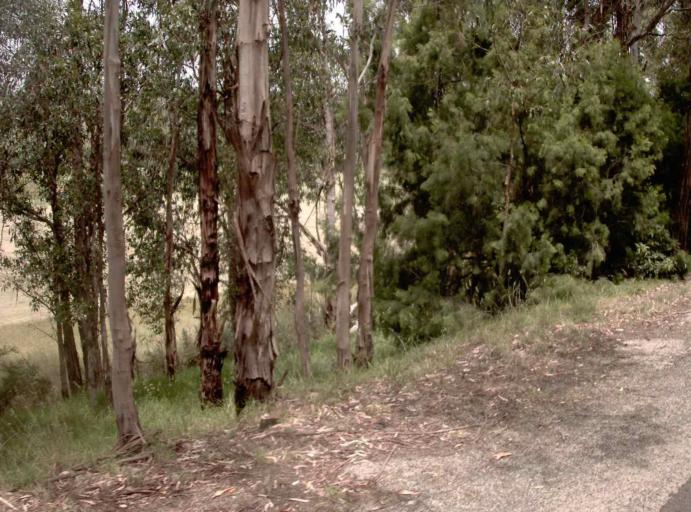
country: AU
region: Victoria
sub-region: Latrobe
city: Traralgon
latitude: -38.4623
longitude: 146.7222
